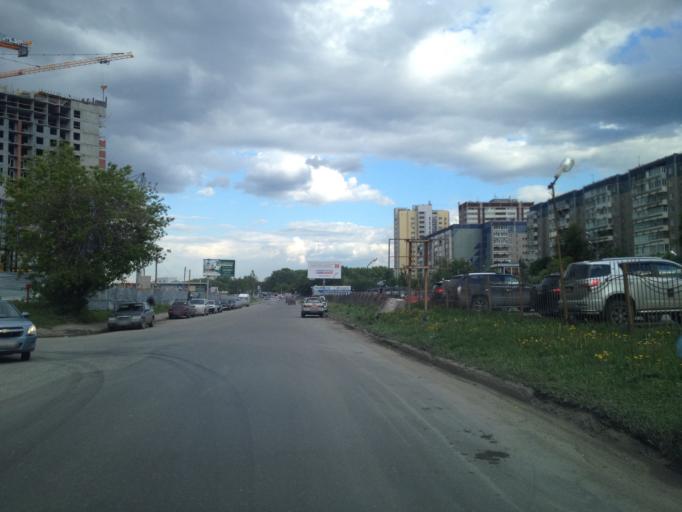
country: RU
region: Sverdlovsk
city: Sovkhoznyy
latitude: 56.8005
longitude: 60.5892
